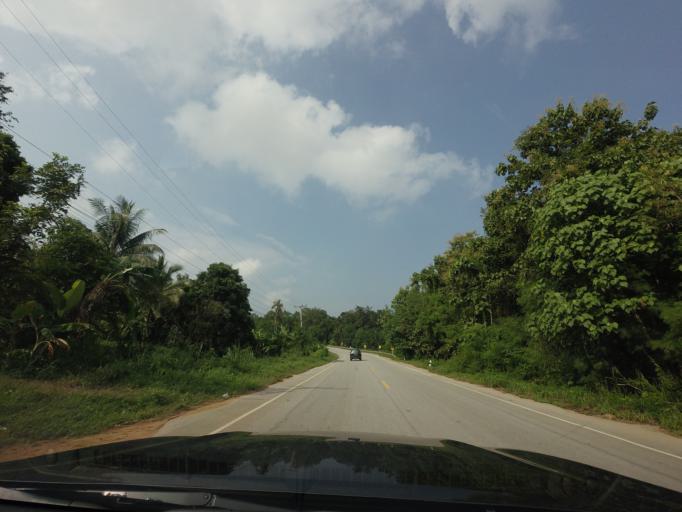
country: TH
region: Loei
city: Chiang Khan
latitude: 17.8873
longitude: 101.6177
